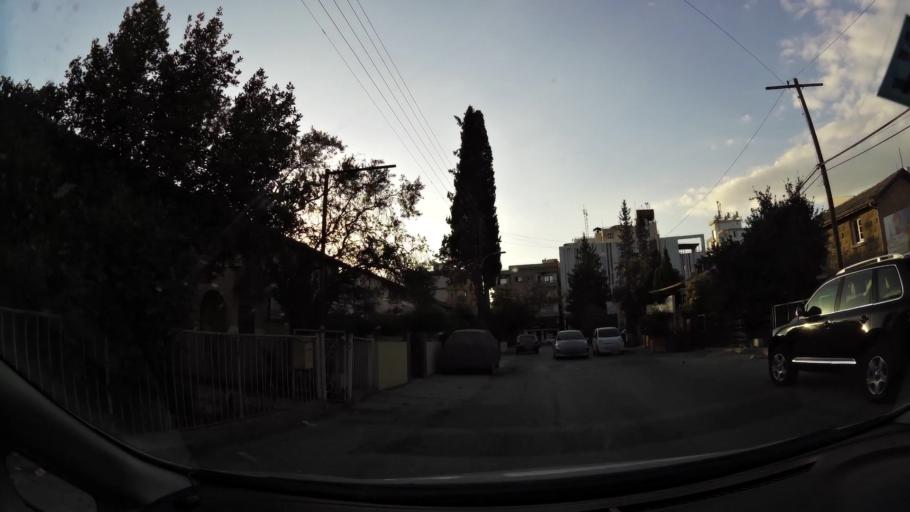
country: CY
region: Lefkosia
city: Nicosia
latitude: 35.1876
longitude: 33.3667
